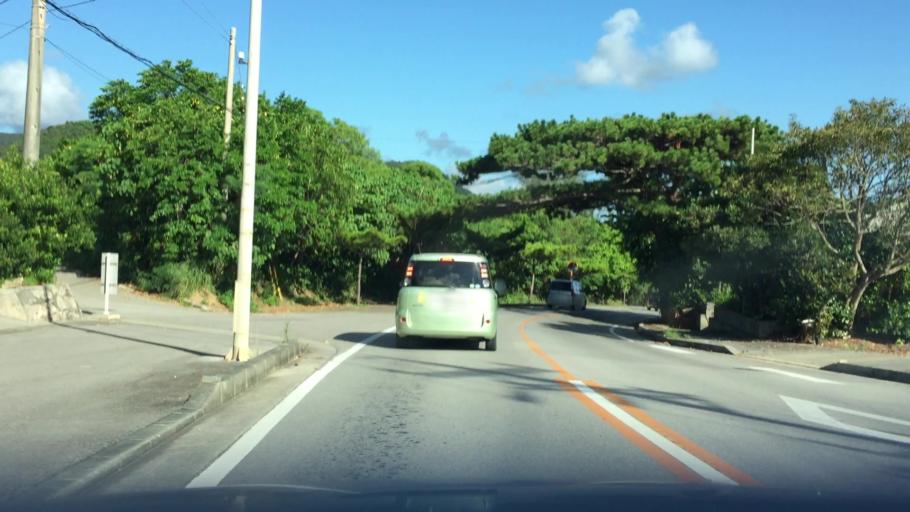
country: JP
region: Okinawa
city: Ishigaki
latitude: 24.4391
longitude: 124.1187
